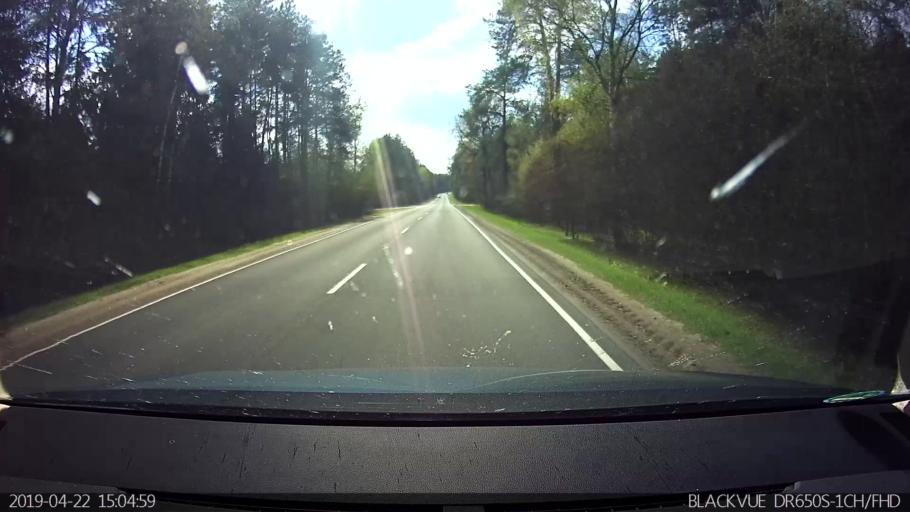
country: BY
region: Brest
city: Kamyanyets
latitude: 52.3365
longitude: 23.8797
